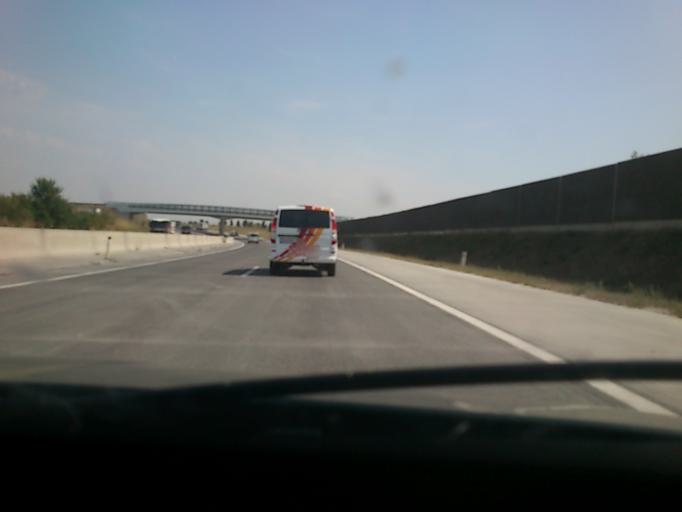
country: AT
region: Lower Austria
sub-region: Politischer Bezirk Ganserndorf
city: Aderklaa
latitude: 48.2672
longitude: 16.5003
